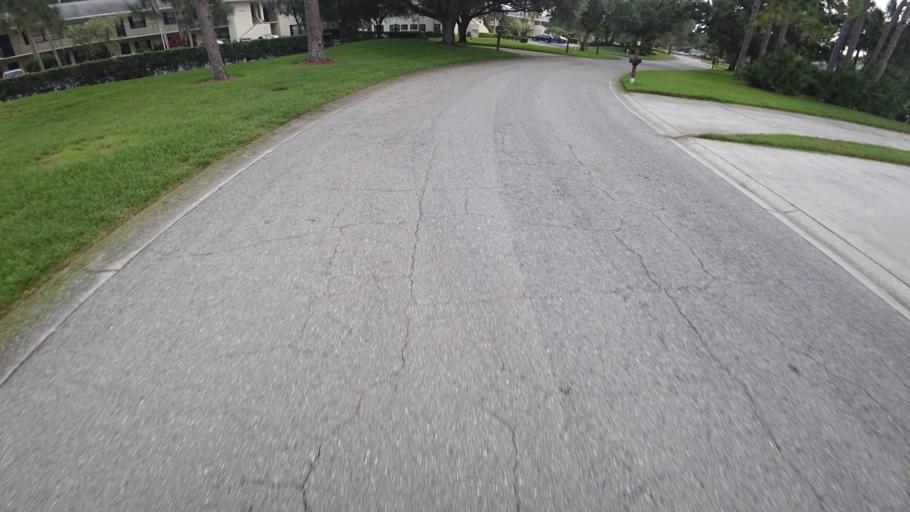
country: US
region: Florida
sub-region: Sarasota County
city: Desoto Lakes
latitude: 27.4131
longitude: -82.4936
